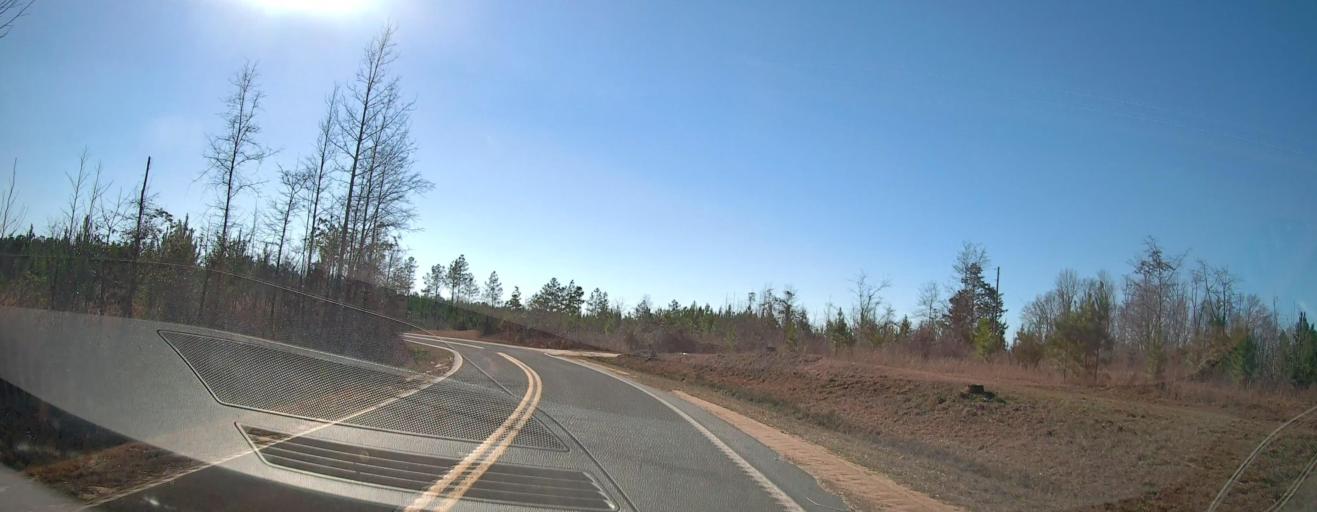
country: US
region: Georgia
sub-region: Taylor County
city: Butler
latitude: 32.6612
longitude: -84.3604
